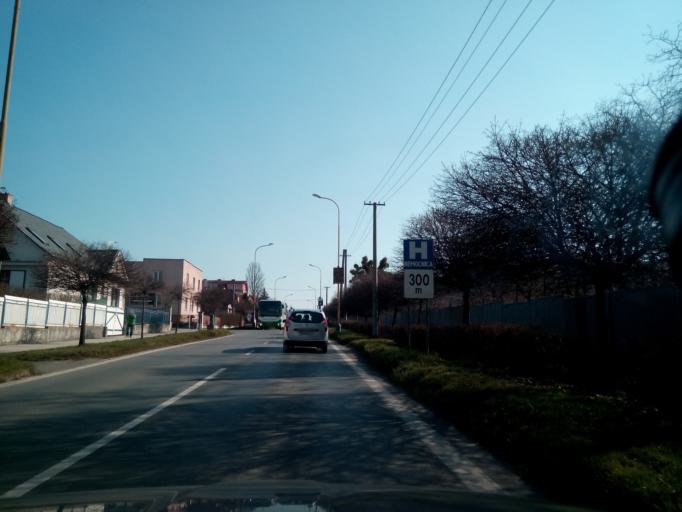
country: SK
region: Presovsky
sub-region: Okres Presov
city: Presov
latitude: 48.9943
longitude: 21.2498
